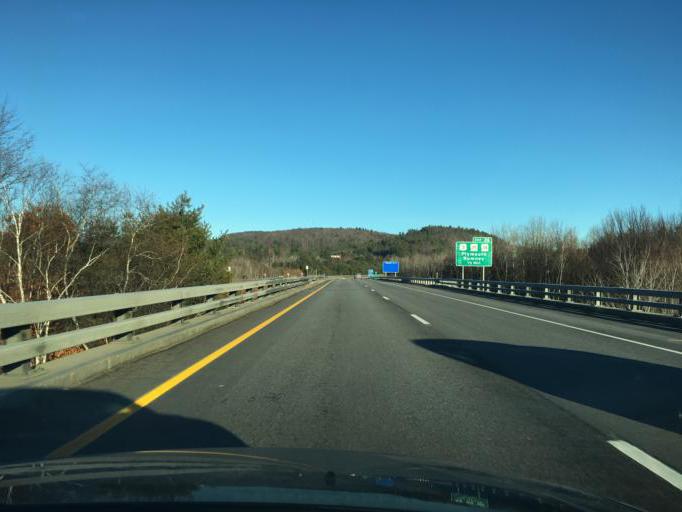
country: US
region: New Hampshire
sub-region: Grafton County
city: Plymouth
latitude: 43.7668
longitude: -71.6809
